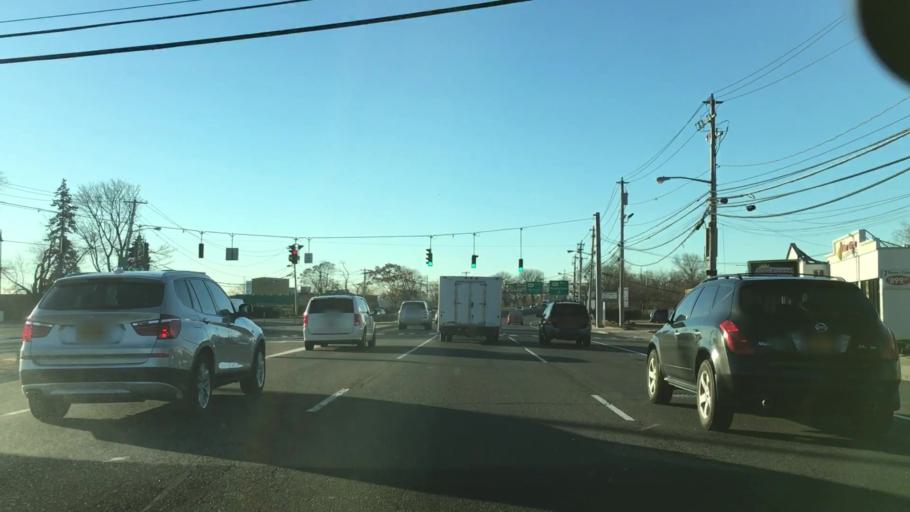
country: US
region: New York
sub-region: Suffolk County
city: East Farmingdale
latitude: 40.7263
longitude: -73.4241
